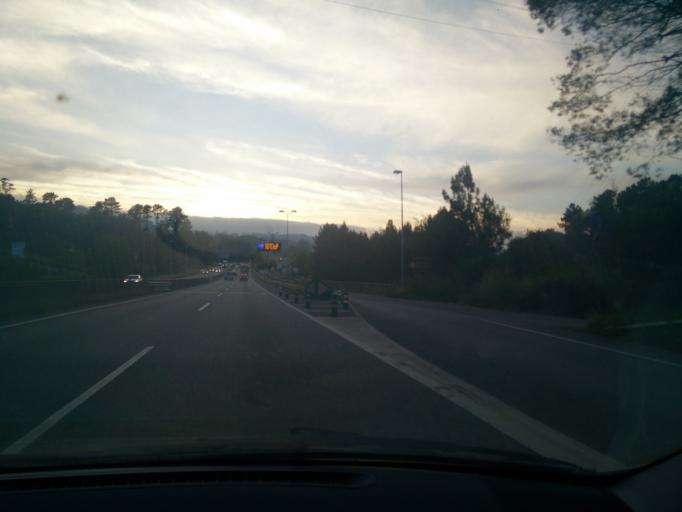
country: ES
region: Galicia
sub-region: Provincia de Pontevedra
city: Porrino
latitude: 42.1820
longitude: -8.6297
